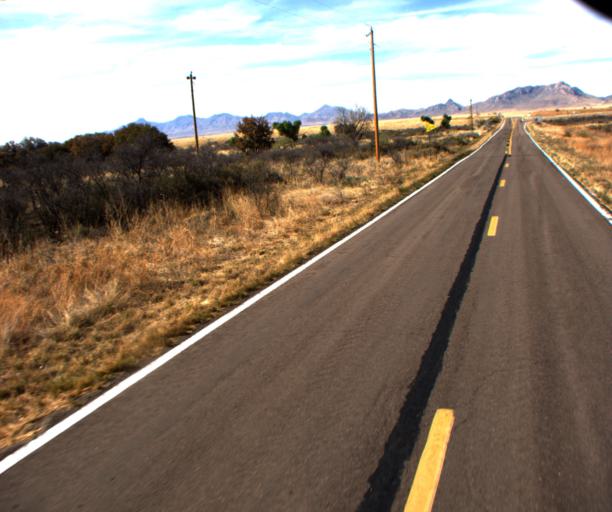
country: US
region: Arizona
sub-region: Cochise County
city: Willcox
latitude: 32.0028
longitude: -109.4400
